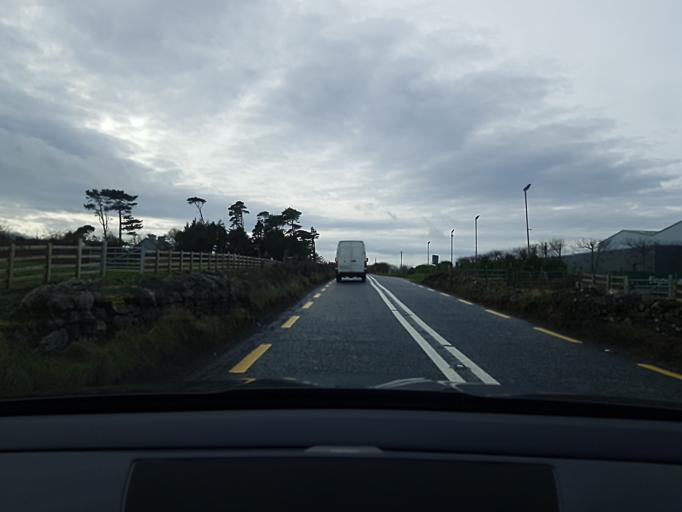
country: IE
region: Connaught
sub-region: Maigh Eo
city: Castlebar
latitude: 53.8375
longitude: -9.2929
